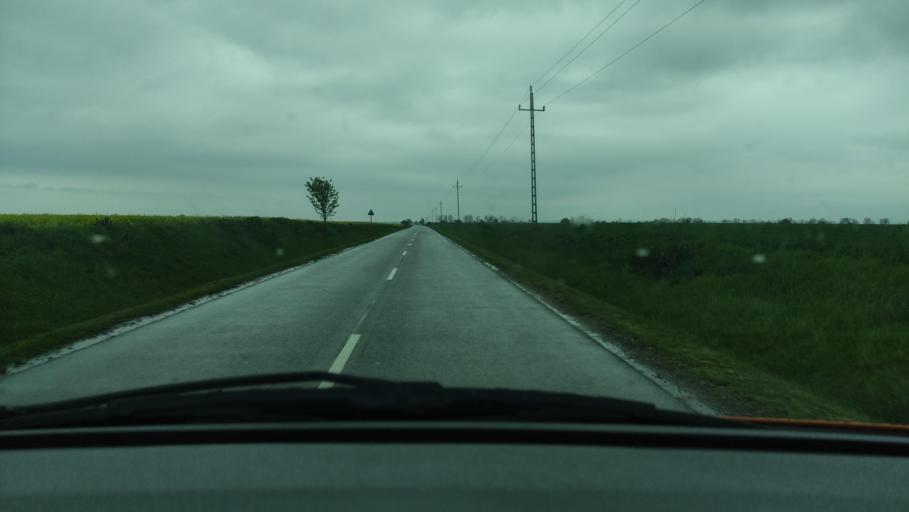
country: HU
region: Baranya
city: Mohacs
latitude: 45.9489
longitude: 18.6849
